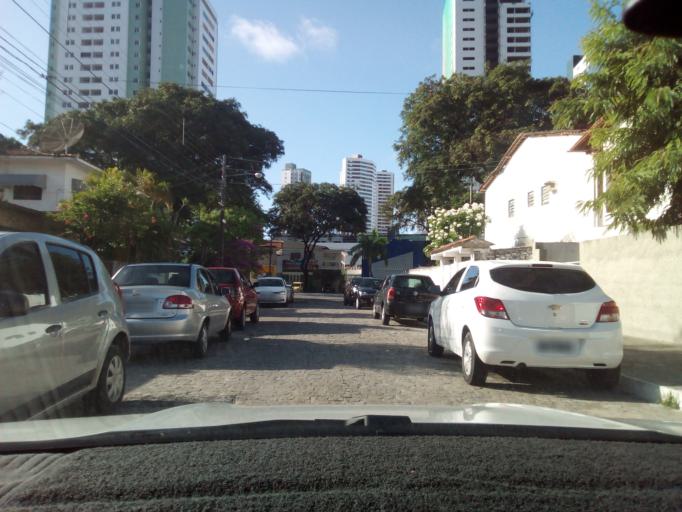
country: BR
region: Paraiba
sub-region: Joao Pessoa
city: Joao Pessoa
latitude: -7.1205
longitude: -34.8376
